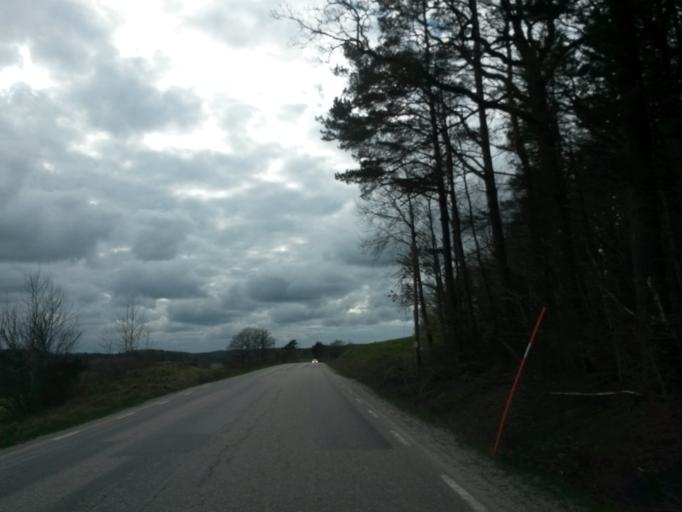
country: SE
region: Vaestra Goetaland
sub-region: Alingsas Kommun
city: Alingsas
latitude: 57.9507
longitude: 12.6201
